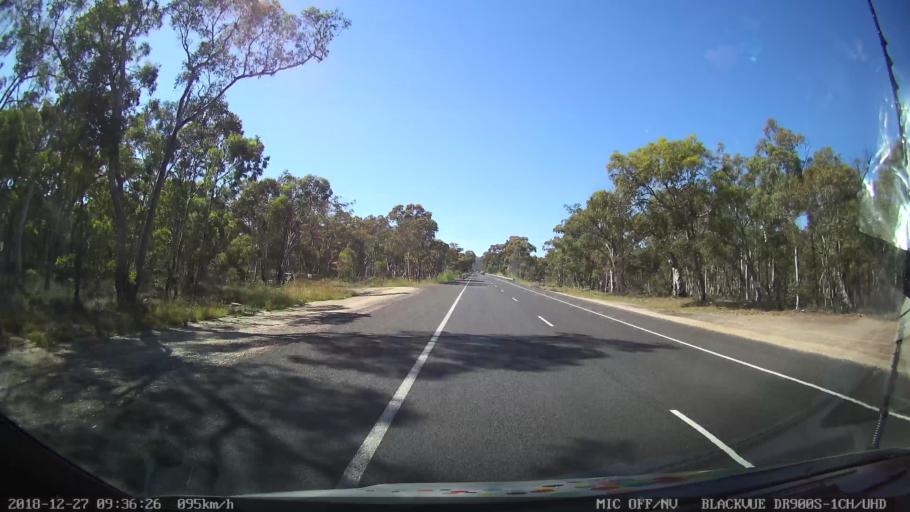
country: AU
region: New South Wales
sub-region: Lithgow
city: Portland
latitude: -33.2522
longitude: 150.0351
